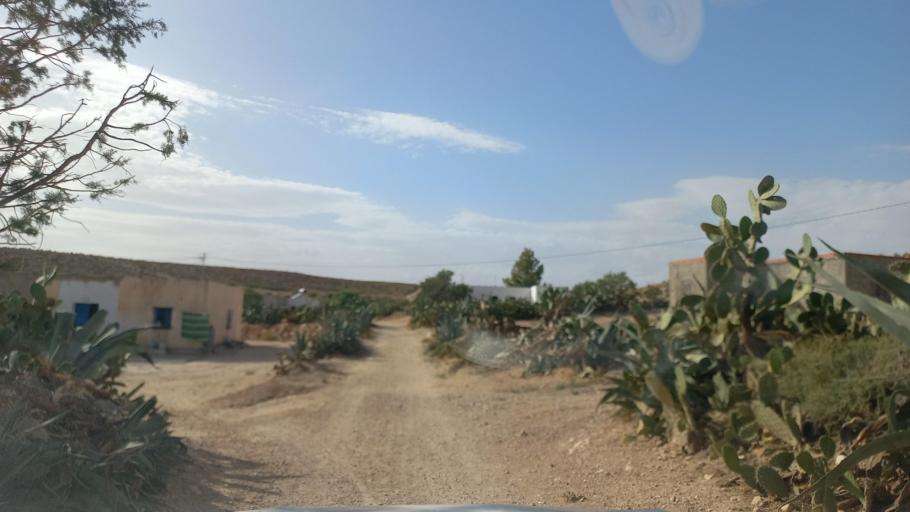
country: TN
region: Al Qasrayn
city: Kasserine
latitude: 35.2579
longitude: 8.9289
